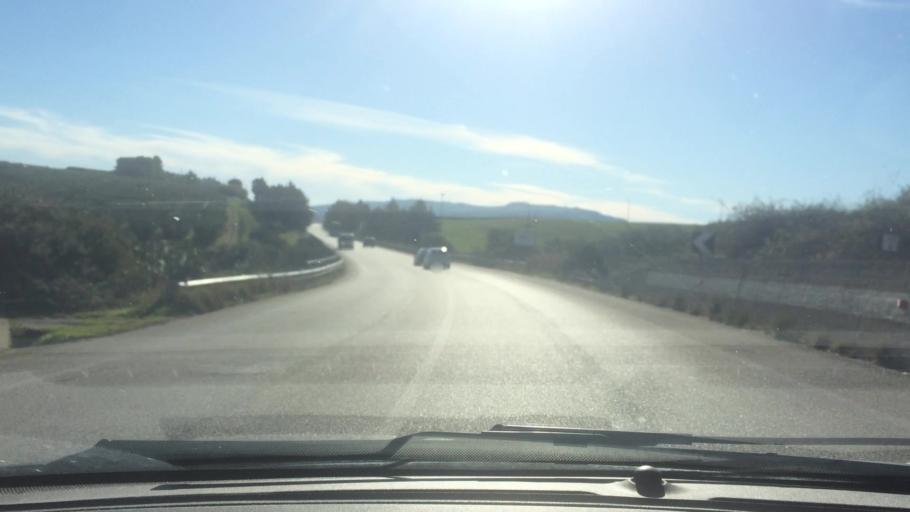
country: IT
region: Basilicate
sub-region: Provincia di Matera
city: Miglionico
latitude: 40.5923
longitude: 16.5734
